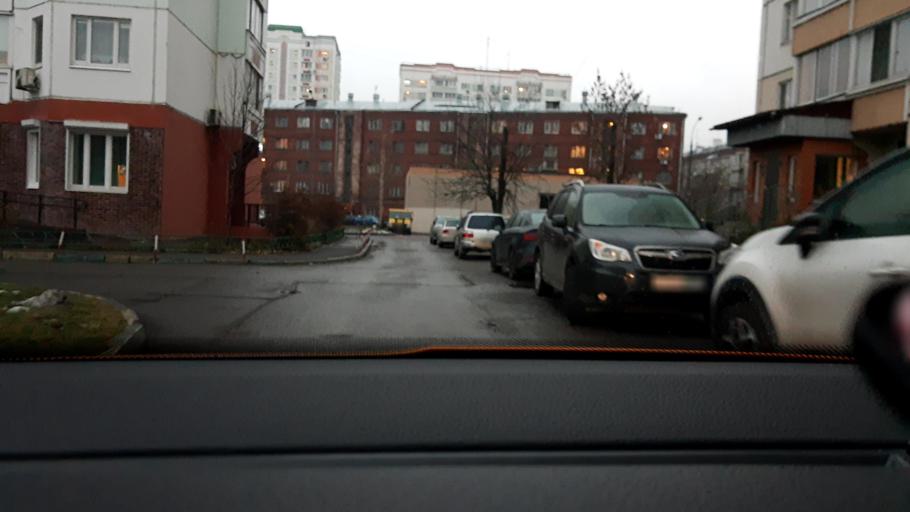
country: RU
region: Moskovskaya
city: Koptevo
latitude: 55.8239
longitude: 37.5080
